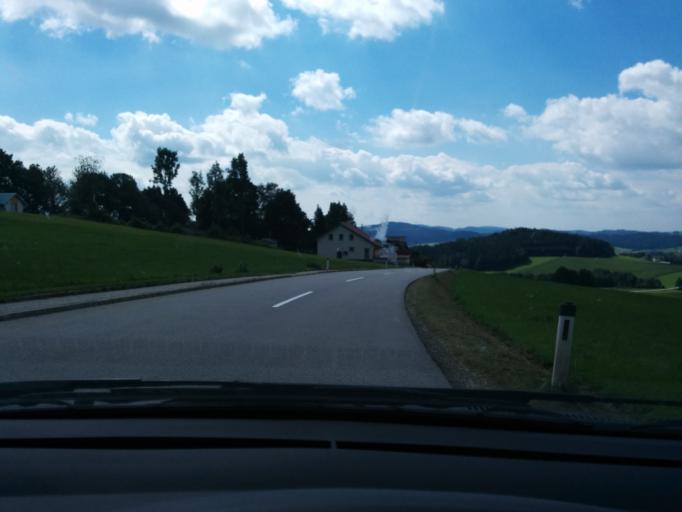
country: AT
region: Upper Austria
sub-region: Politischer Bezirk Rohrbach
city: Ulrichsberg
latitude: 48.7125
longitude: 13.9021
